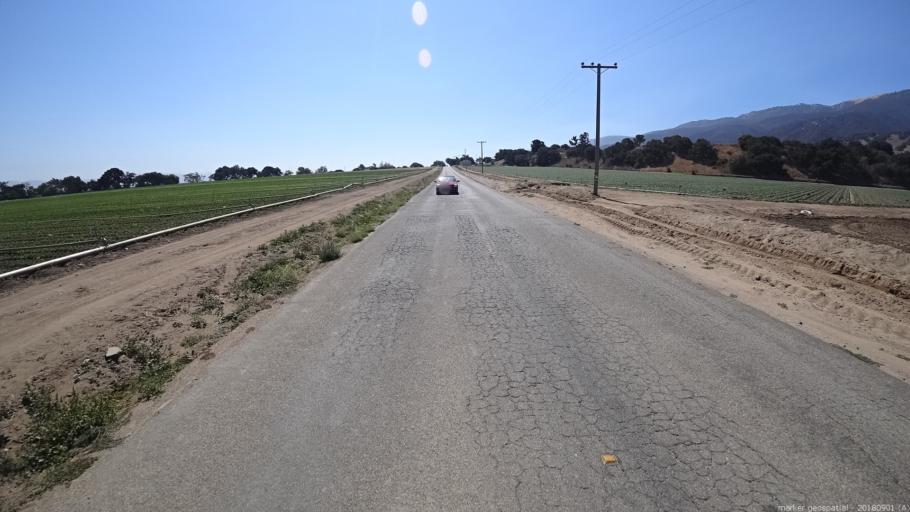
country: US
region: California
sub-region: Monterey County
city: Chualar
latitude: 36.5262
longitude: -121.5256
